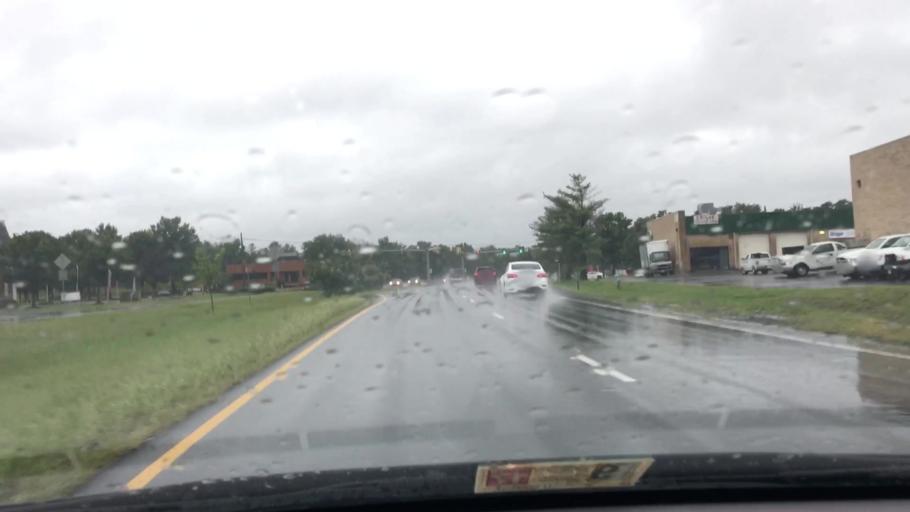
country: US
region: Virginia
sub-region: Loudoun County
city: Sterling
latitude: 38.9932
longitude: -77.4185
